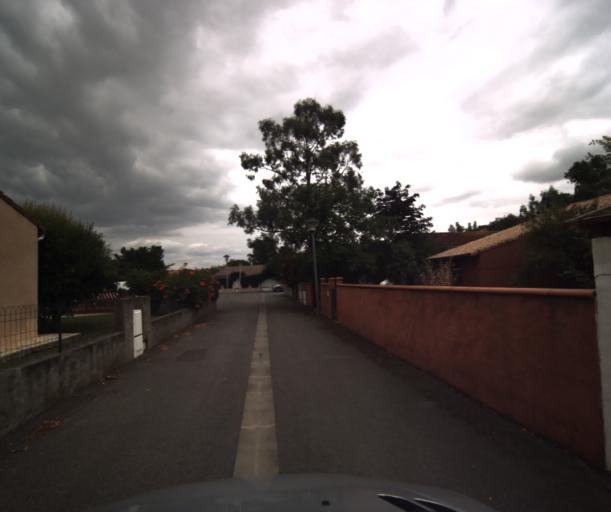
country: FR
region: Midi-Pyrenees
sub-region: Departement de la Haute-Garonne
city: Labarthe-sur-Leze
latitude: 43.4551
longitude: 1.4056
